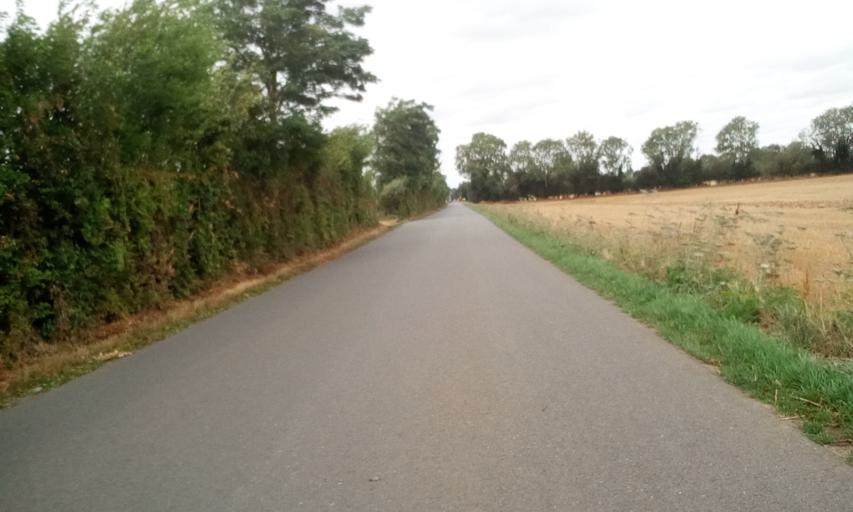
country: FR
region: Lower Normandy
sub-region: Departement du Calvados
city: Fontaine-Etoupefour
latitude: 49.1319
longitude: -0.4647
